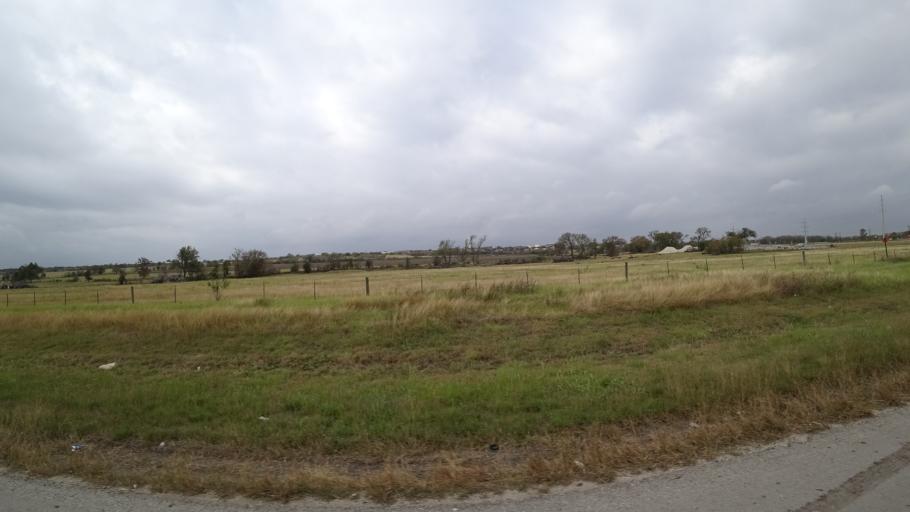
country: US
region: Texas
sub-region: Travis County
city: Pflugerville
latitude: 30.4505
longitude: -97.5952
